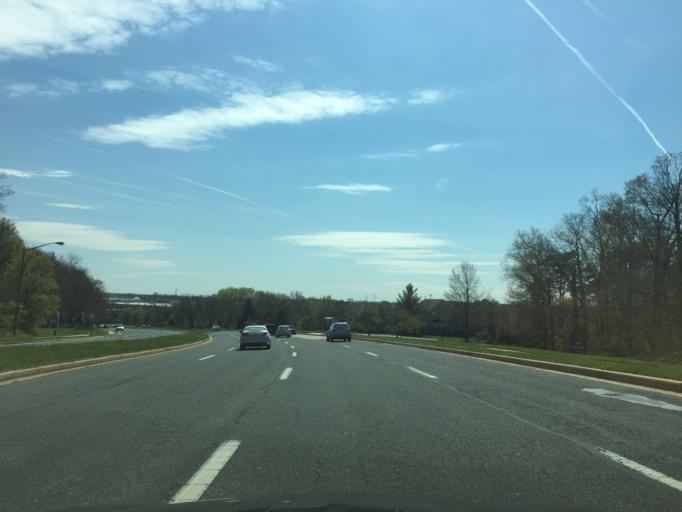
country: US
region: Maryland
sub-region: Baltimore County
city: Rossville
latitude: 39.3453
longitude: -76.4873
